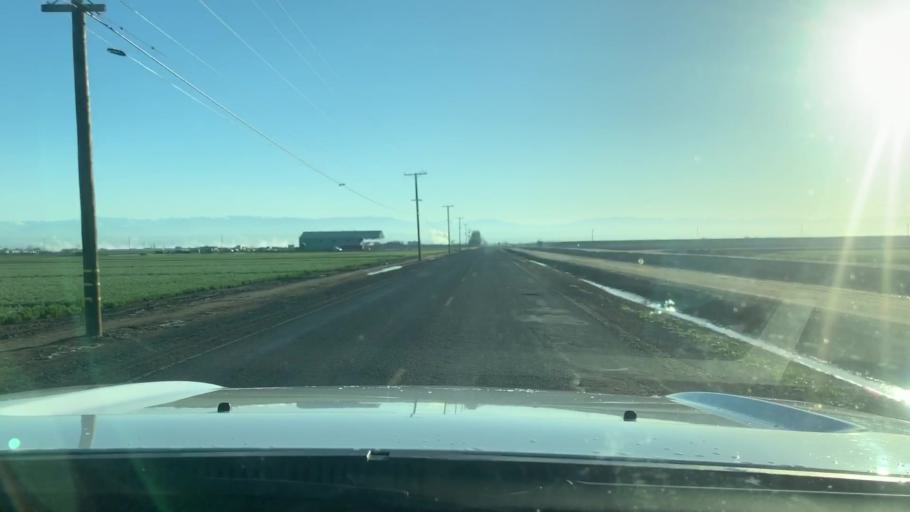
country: US
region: California
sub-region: Tulare County
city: Tulare
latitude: 36.1818
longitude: -119.3900
